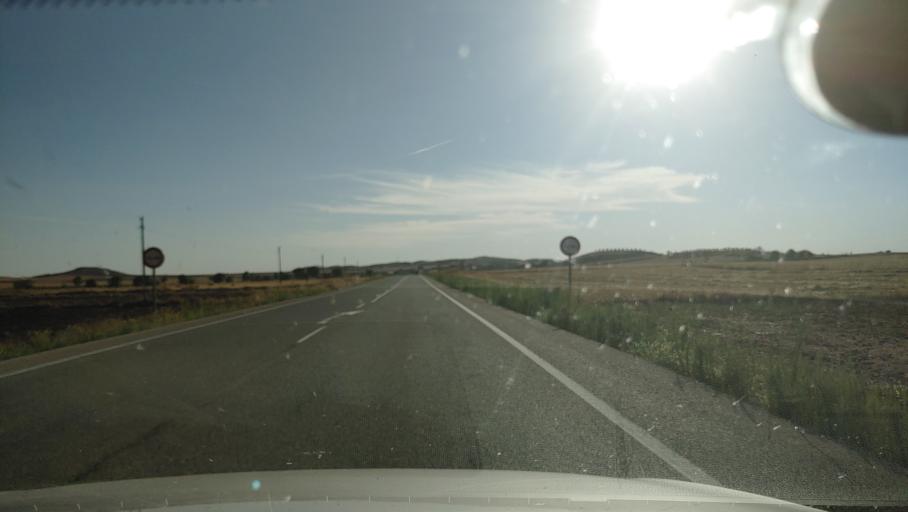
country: ES
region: Castille-La Mancha
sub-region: Provincia de Ciudad Real
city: Fuenllana
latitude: 38.7602
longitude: -2.9426
